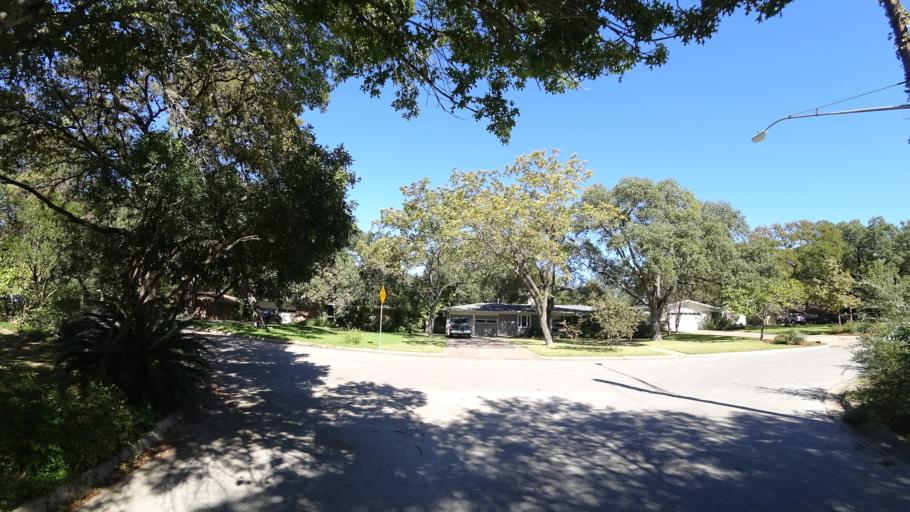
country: US
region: Texas
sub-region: Travis County
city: Austin
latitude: 30.3198
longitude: -97.7479
